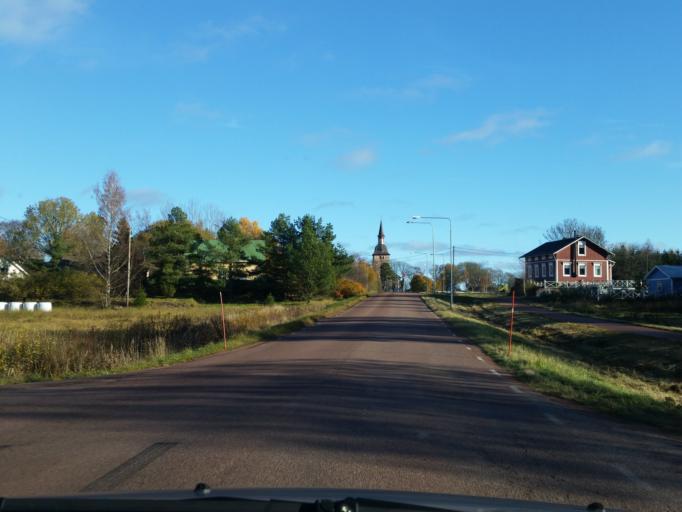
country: AX
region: Alands landsbygd
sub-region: Jomala
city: Jomala
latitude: 60.1547
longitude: 19.9397
